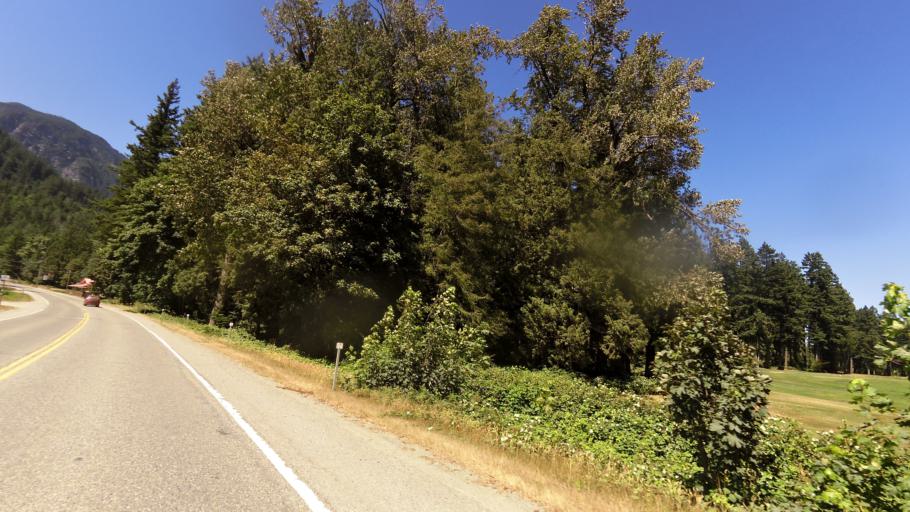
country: CA
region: British Columbia
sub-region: Fraser Valley Regional District
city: Chilliwack
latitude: 49.2500
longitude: -121.9500
